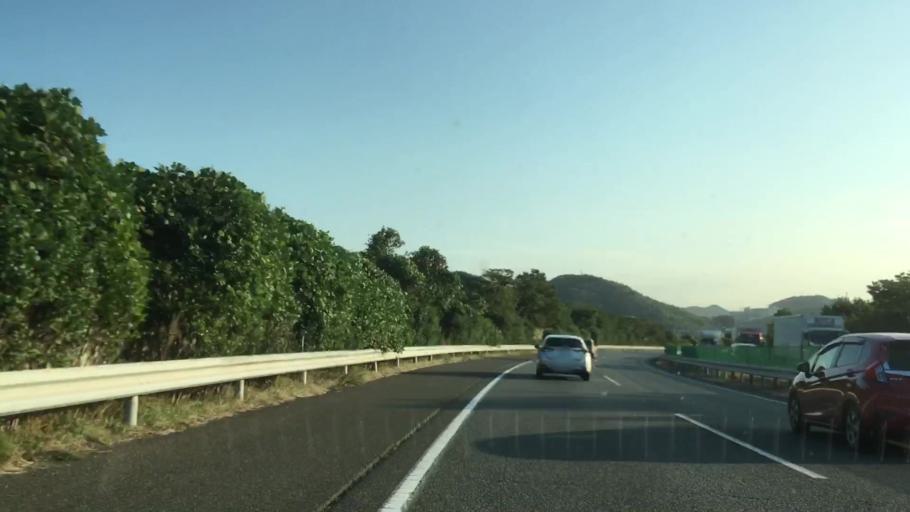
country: JP
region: Yamaguchi
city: Shimonoseki
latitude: 34.0173
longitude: 130.9576
